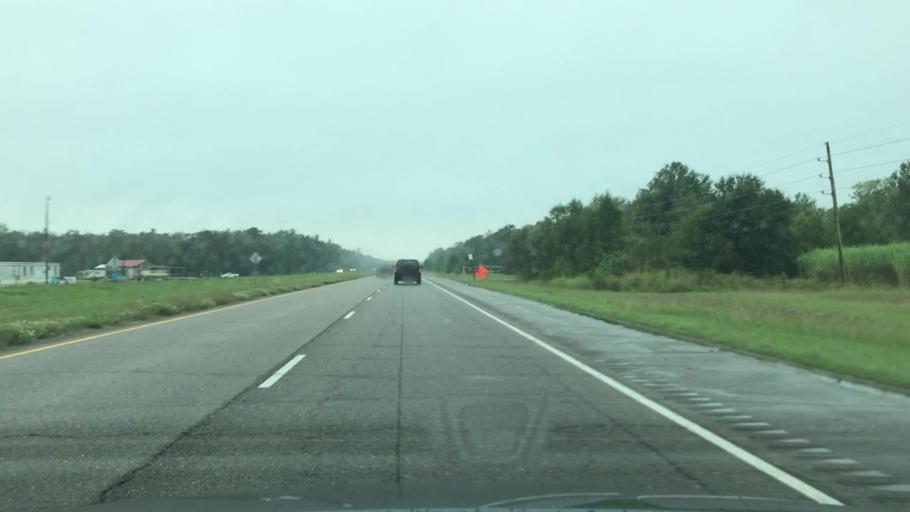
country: US
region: Louisiana
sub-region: Lafourche Parish
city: Raceland
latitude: 29.7384
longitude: -90.5576
